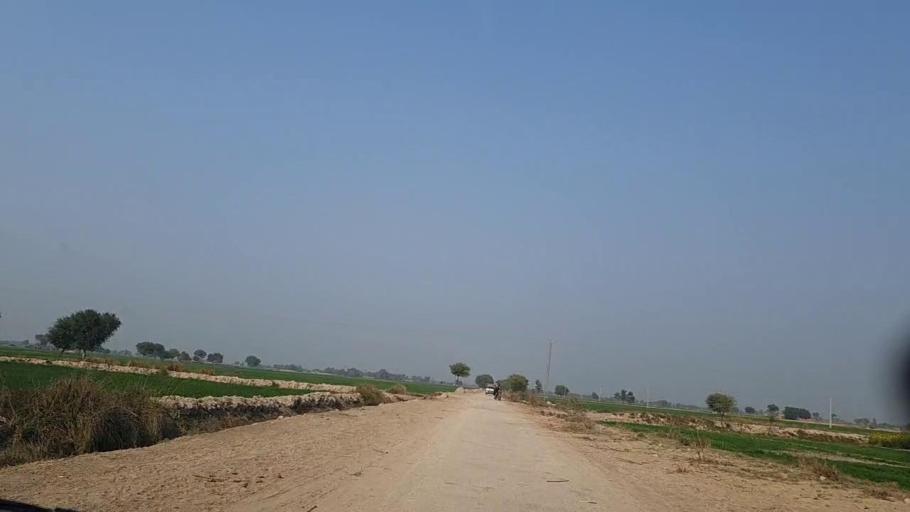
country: PK
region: Sindh
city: Sann
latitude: 26.1882
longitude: 68.1120
